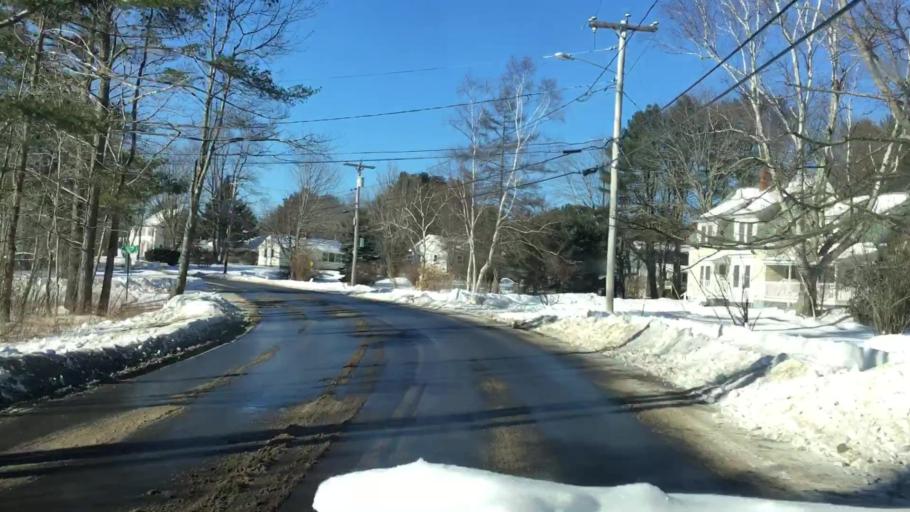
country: US
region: Maine
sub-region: Sagadahoc County
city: Topsham
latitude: 43.9276
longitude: -69.9745
